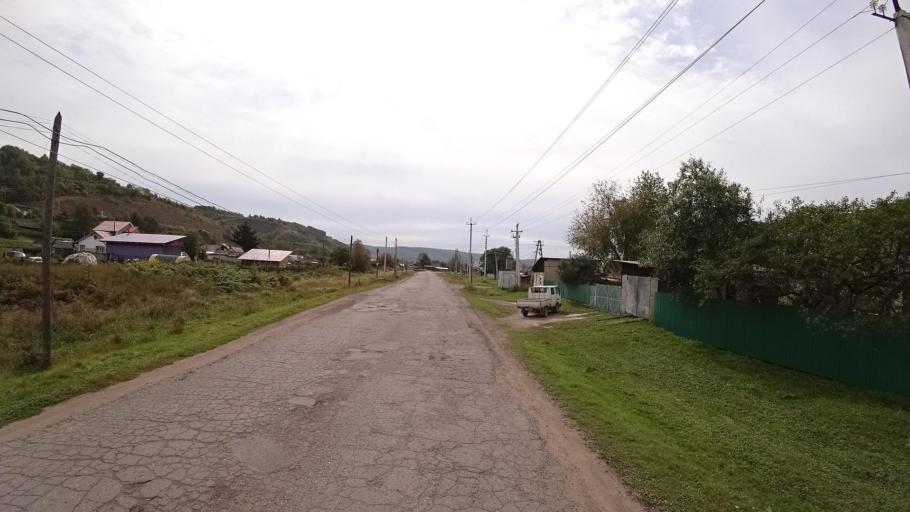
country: RU
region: Jewish Autonomous Oblast
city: Khingansk
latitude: 49.0018
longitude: 131.0542
